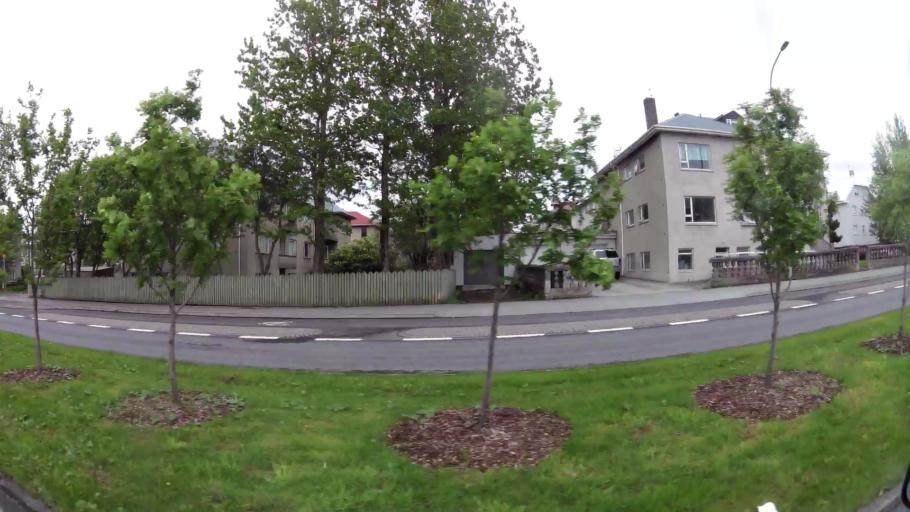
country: IS
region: Capital Region
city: Reykjavik
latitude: 64.1326
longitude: -21.9125
